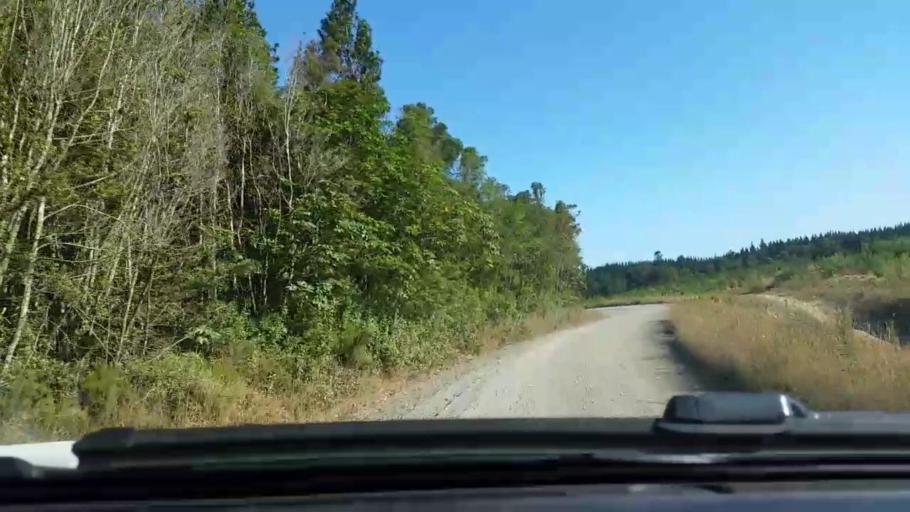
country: NZ
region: Bay of Plenty
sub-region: Kawerau District
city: Kawerau
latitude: -37.9931
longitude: 176.5365
